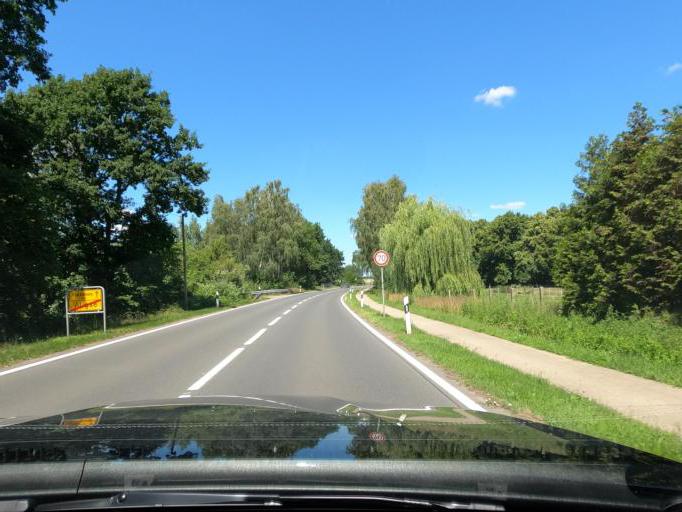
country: DE
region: Lower Saxony
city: Lehrte
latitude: 52.4041
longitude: 9.9740
